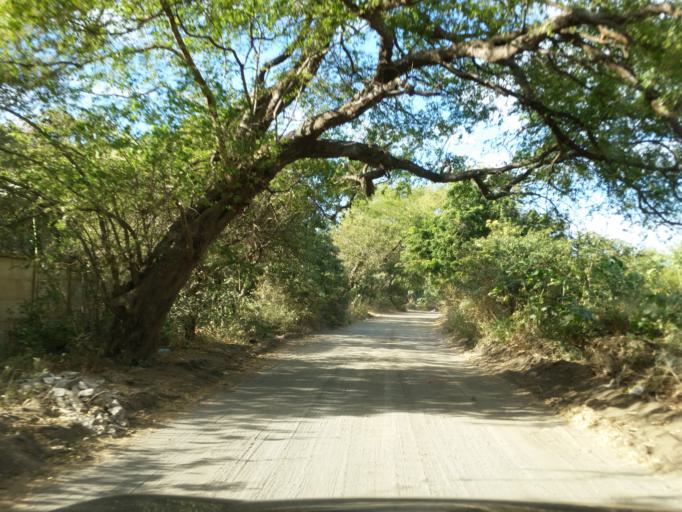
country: NI
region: Managua
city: Managua
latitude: 12.1007
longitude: -86.2607
